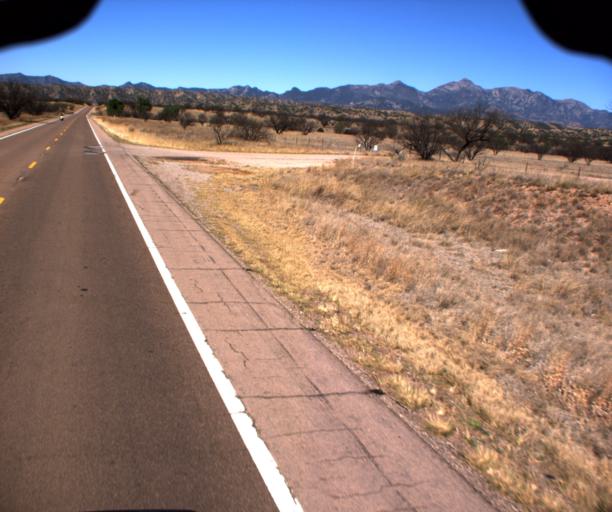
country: US
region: Arizona
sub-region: Pima County
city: Corona de Tucson
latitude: 31.6594
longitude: -110.6941
